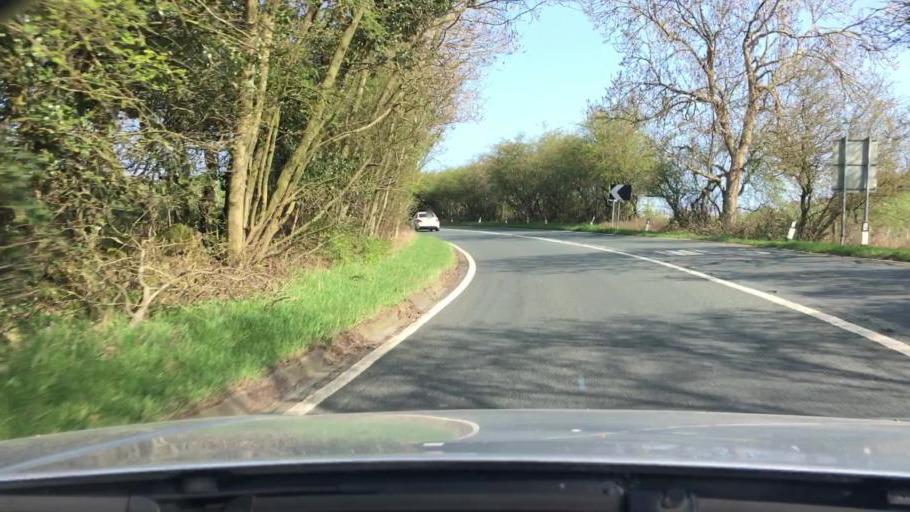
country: GB
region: England
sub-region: North Yorkshire
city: Pannal
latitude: 53.9392
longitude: -1.5367
